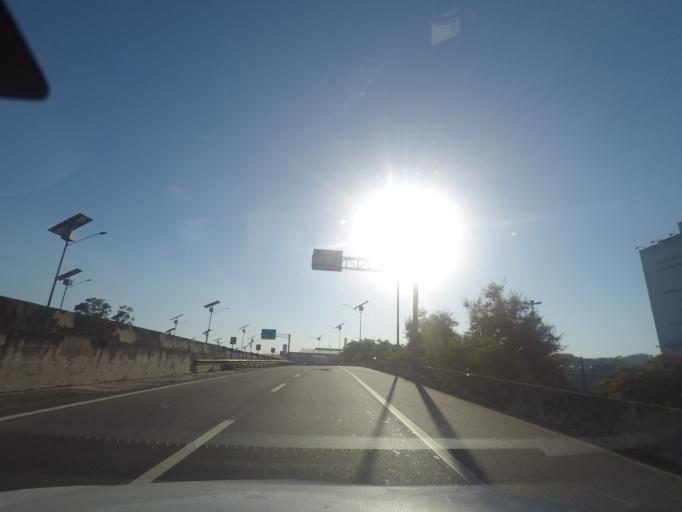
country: BR
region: Rio de Janeiro
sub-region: Duque De Caxias
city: Duque de Caxias
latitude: -22.6724
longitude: -43.2831
